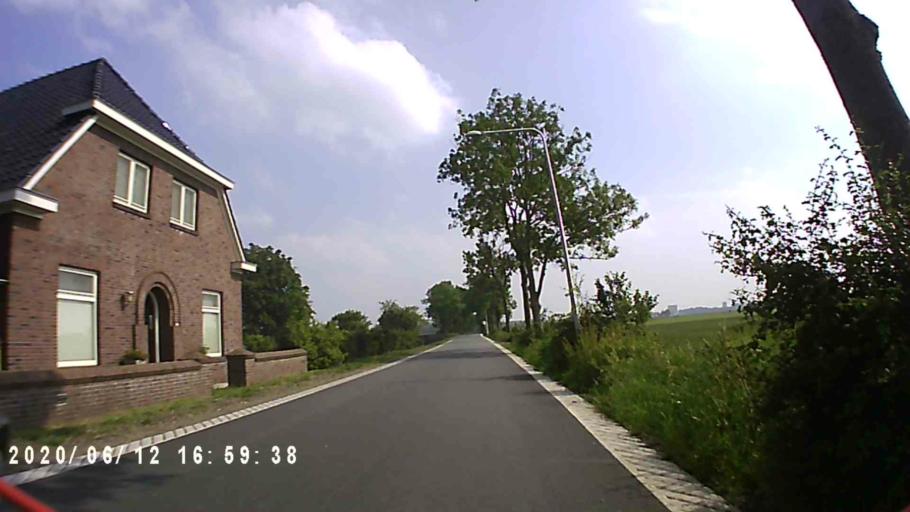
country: NL
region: Groningen
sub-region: Gemeente Groningen
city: Korrewegwijk
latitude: 53.2630
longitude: 6.5668
